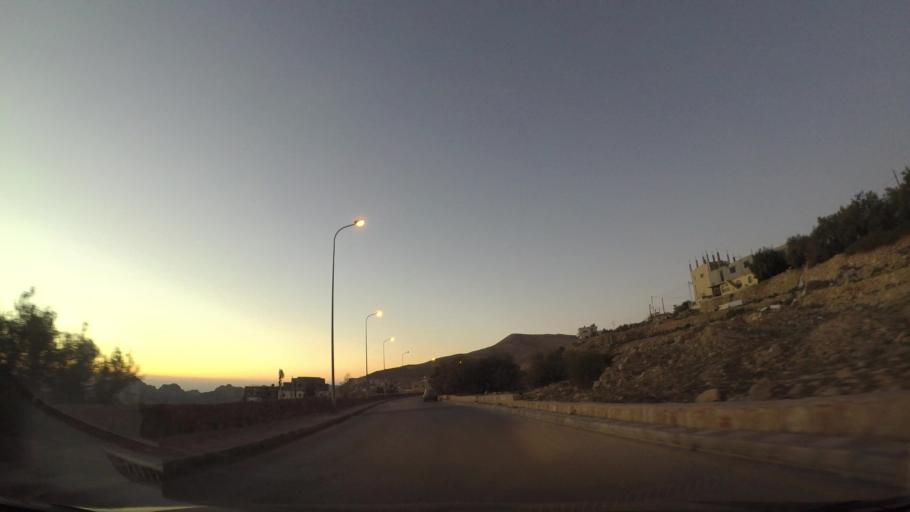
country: JO
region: Ma'an
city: Petra
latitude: 30.3217
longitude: 35.4818
